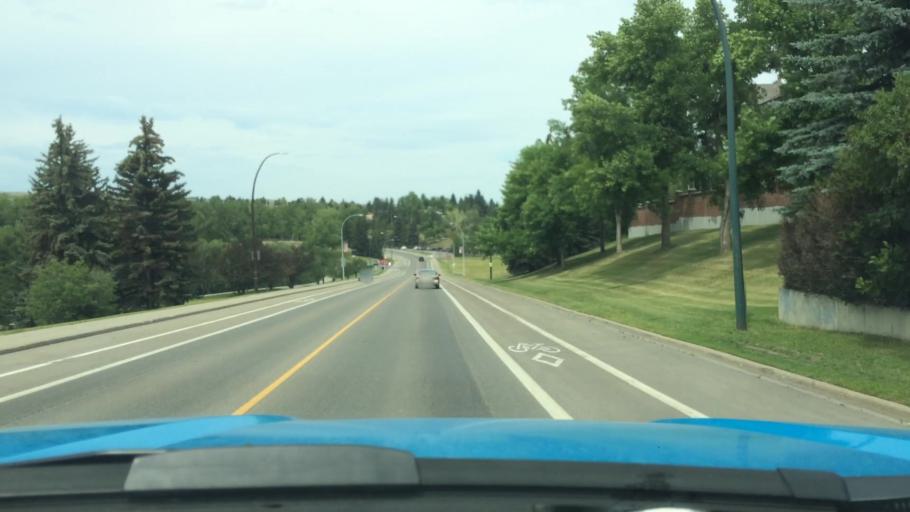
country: CA
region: Alberta
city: Calgary
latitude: 51.0740
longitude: -114.0846
